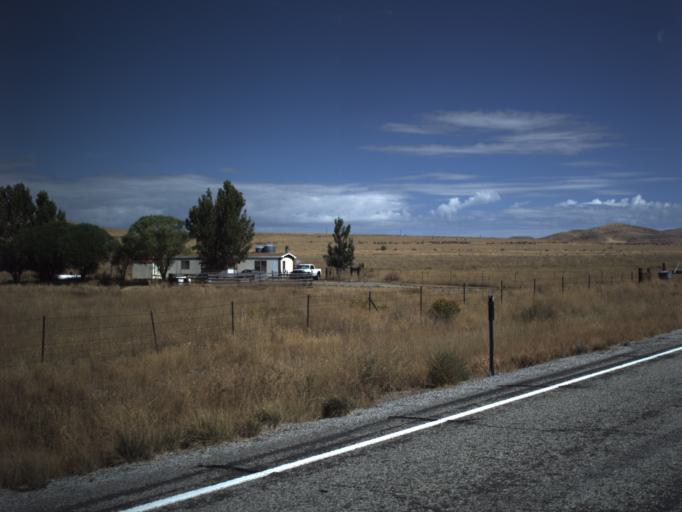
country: US
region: Utah
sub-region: Box Elder County
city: Garland
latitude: 41.7867
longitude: -112.4297
